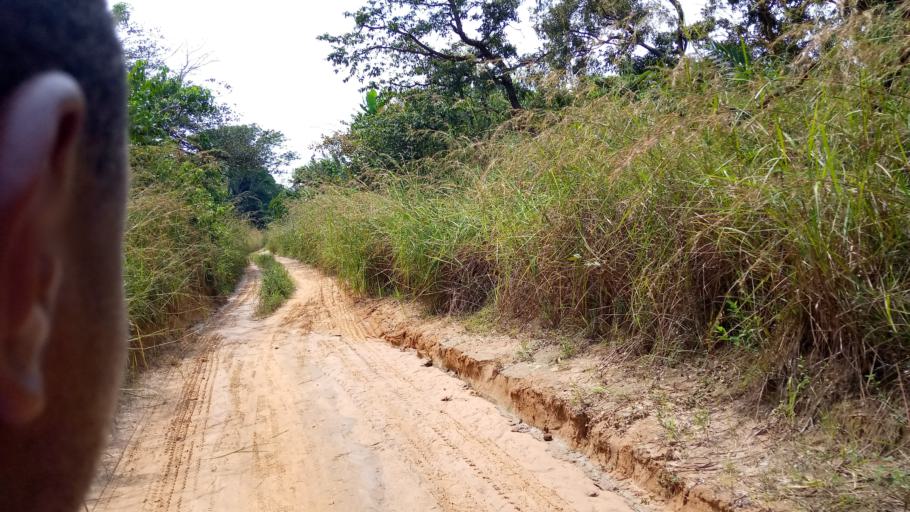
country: CD
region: Bandundu
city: Bandundu
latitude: -4.1481
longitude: 17.4146
